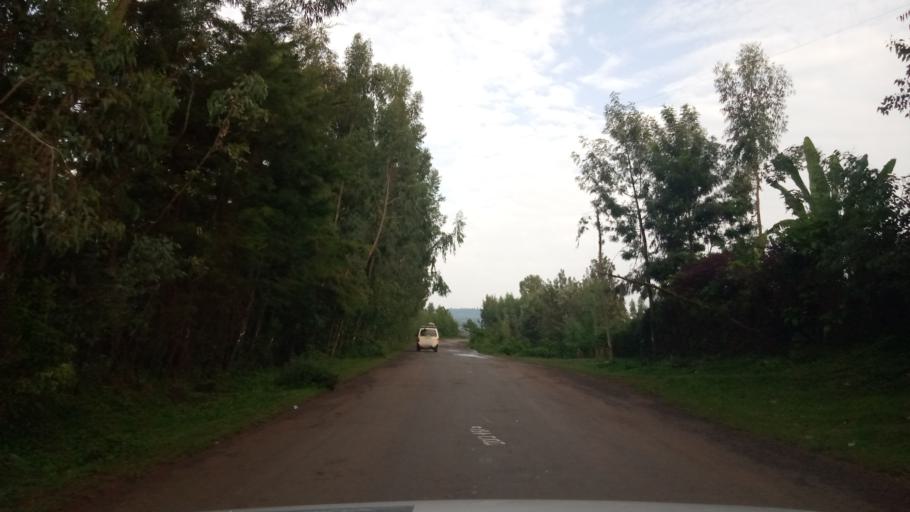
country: ET
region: Oromiya
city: Jima
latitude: 7.7416
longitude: 36.7435
